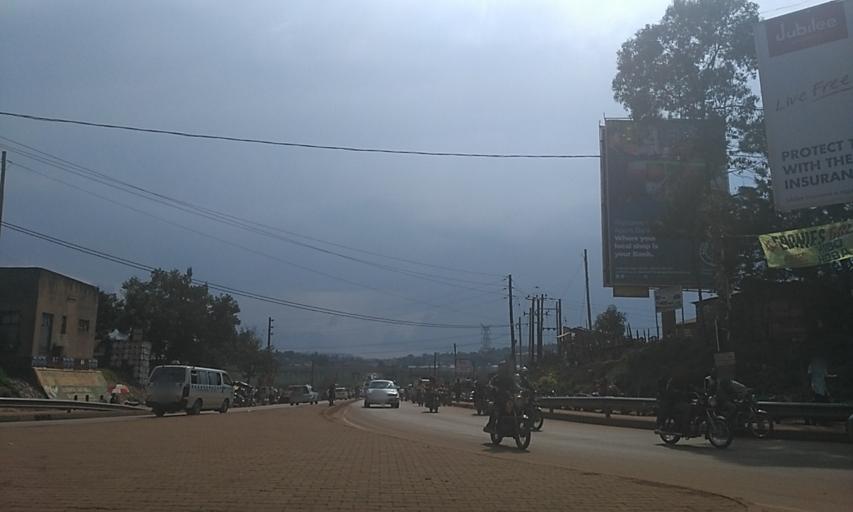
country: UG
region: Central Region
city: Kampala Central Division
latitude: 0.3066
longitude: 32.5164
